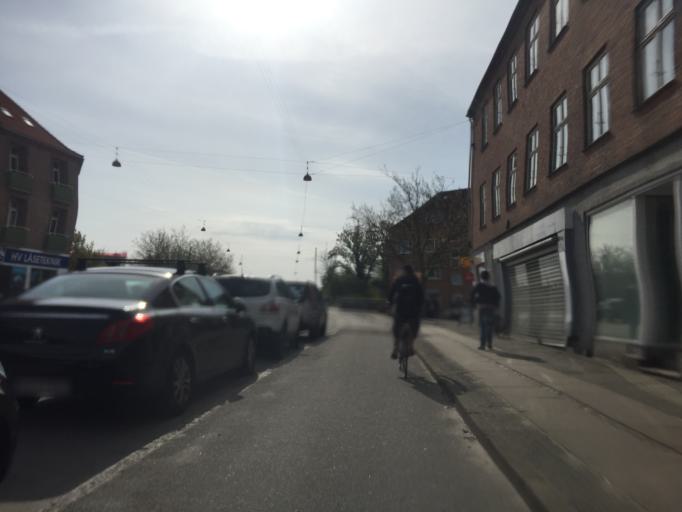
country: DK
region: Capital Region
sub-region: Kobenhavn
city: Vanlose
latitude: 55.6695
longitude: 12.4923
